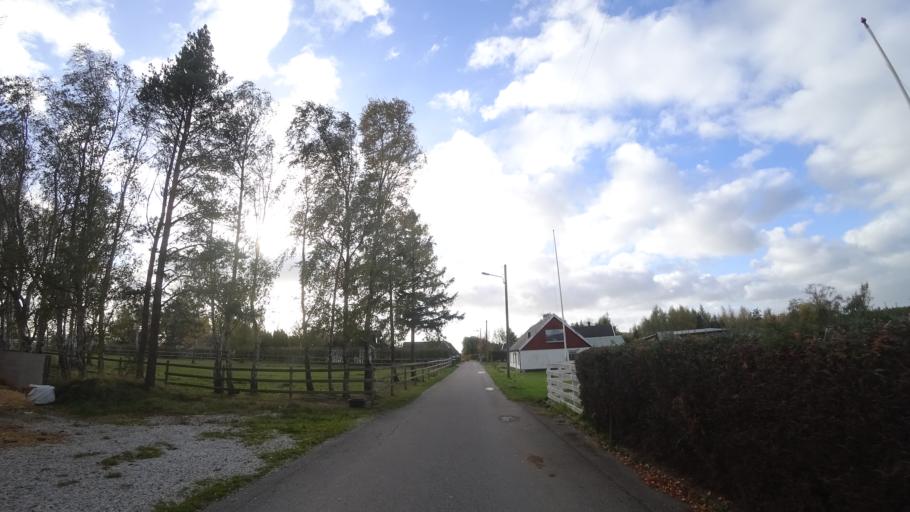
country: SE
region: Skane
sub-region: Staffanstorps Kommun
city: Staffanstorp
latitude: 55.6272
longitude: 13.2134
